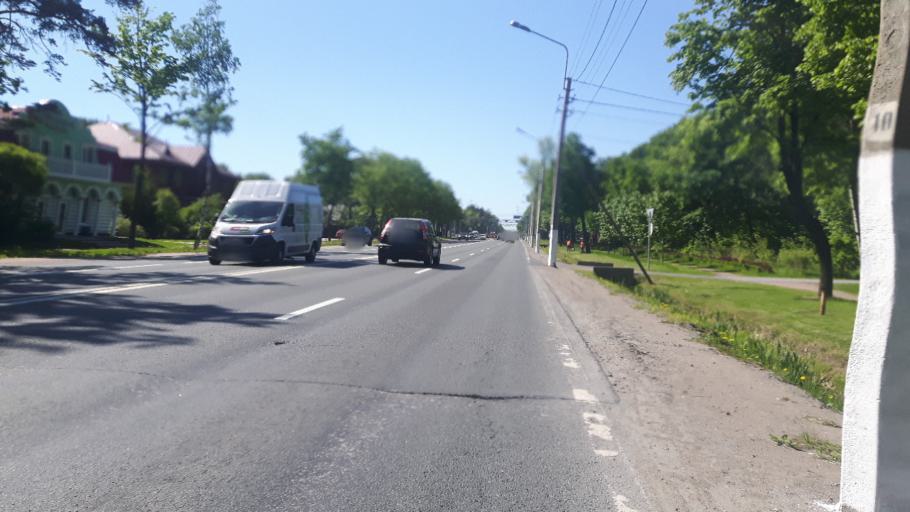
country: RU
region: Leningrad
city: Ol'gino
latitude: 59.8741
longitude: 29.9512
